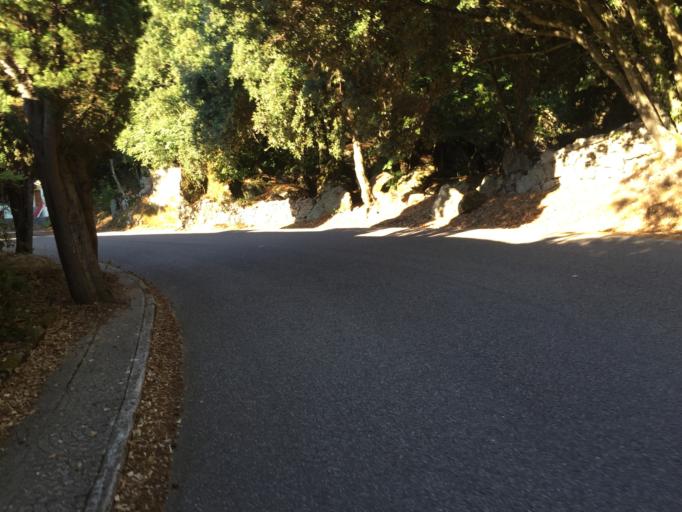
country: IT
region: Sardinia
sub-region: Provincia di Olbia-Tempio
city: Aggius
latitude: 40.9336
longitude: 9.0661
